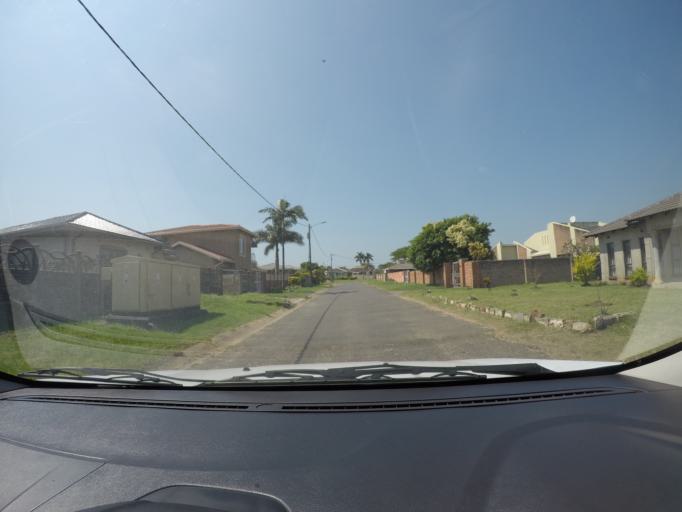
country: ZA
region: KwaZulu-Natal
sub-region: uThungulu District Municipality
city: eSikhawini
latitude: -28.8668
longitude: 31.9126
